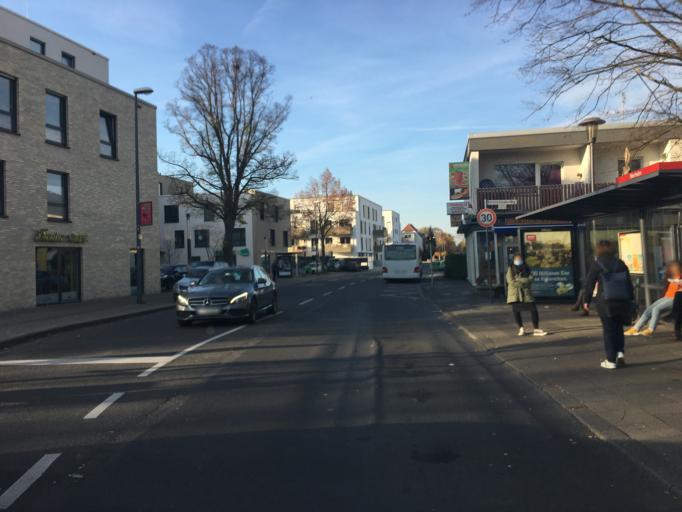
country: DE
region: North Rhine-Westphalia
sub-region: Regierungsbezirk Koln
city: Merheim
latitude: 50.9440
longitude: 7.0481
